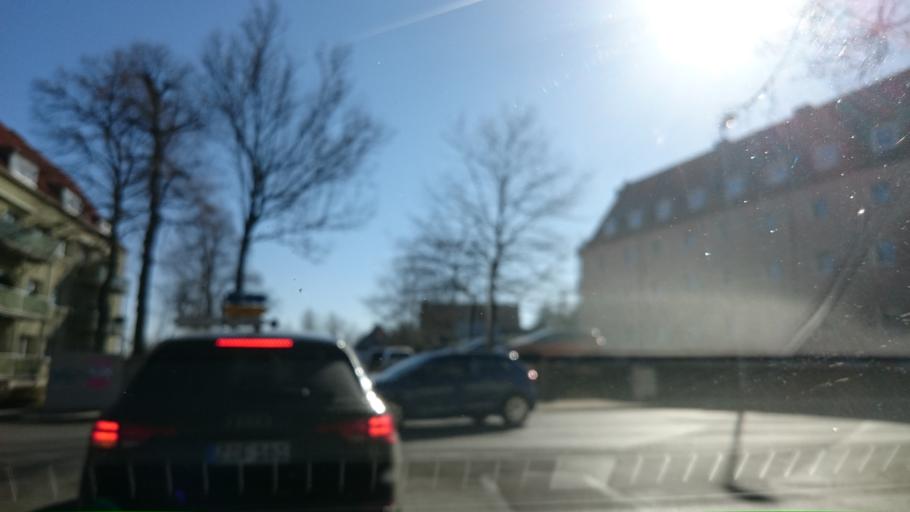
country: DE
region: Saxony
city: Lichtentanne
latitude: 50.7225
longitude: 12.4417
